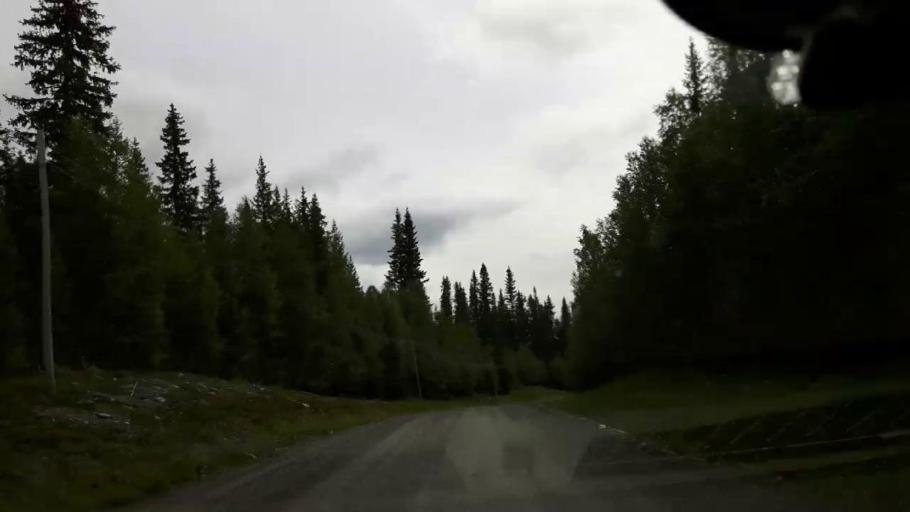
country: SE
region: Jaemtland
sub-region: Krokoms Kommun
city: Valla
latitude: 63.7194
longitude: 13.8579
